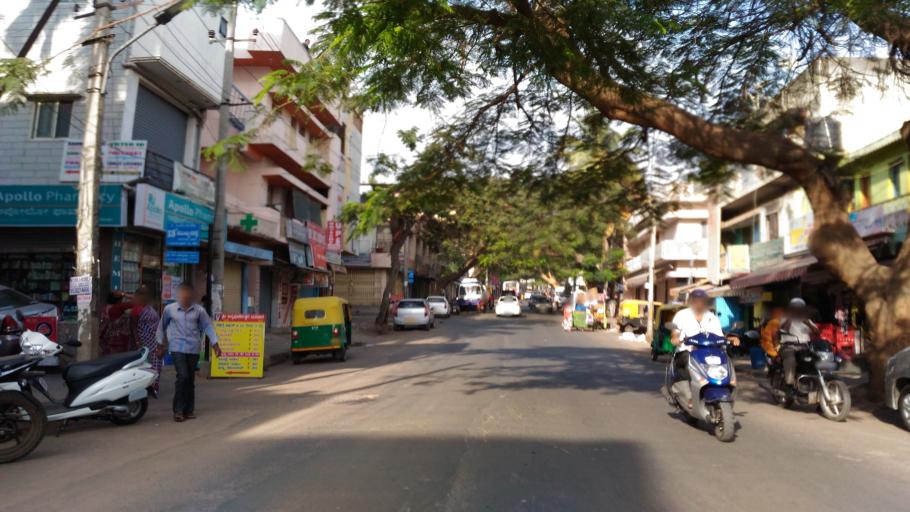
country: IN
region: Karnataka
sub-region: Bangalore Urban
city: Bangalore
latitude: 12.9422
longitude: 77.5499
